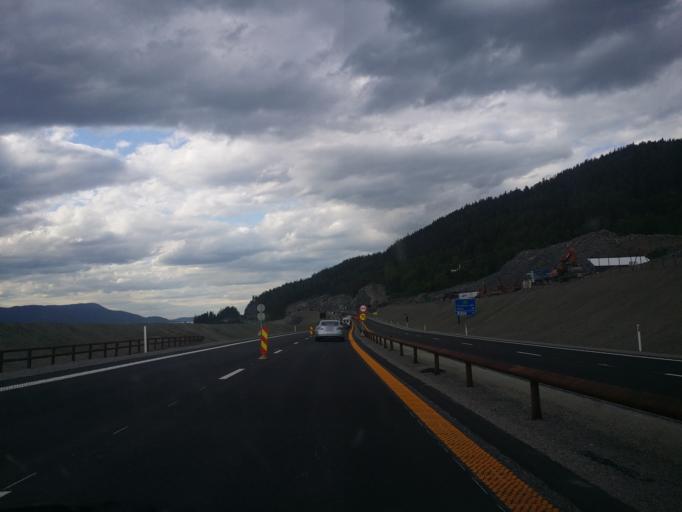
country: NO
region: Akershus
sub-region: Eidsvoll
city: Eidsvoll
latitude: 60.4228
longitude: 11.2404
